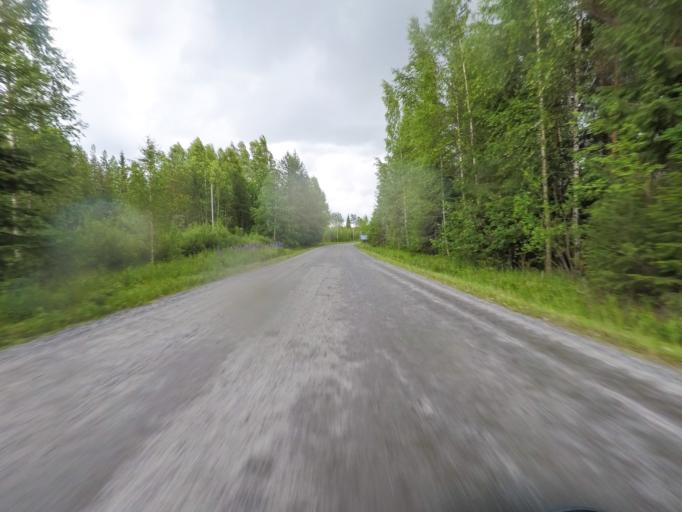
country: FI
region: Central Finland
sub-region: Jyvaeskylae
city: Hankasalmi
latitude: 62.3886
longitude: 26.6036
